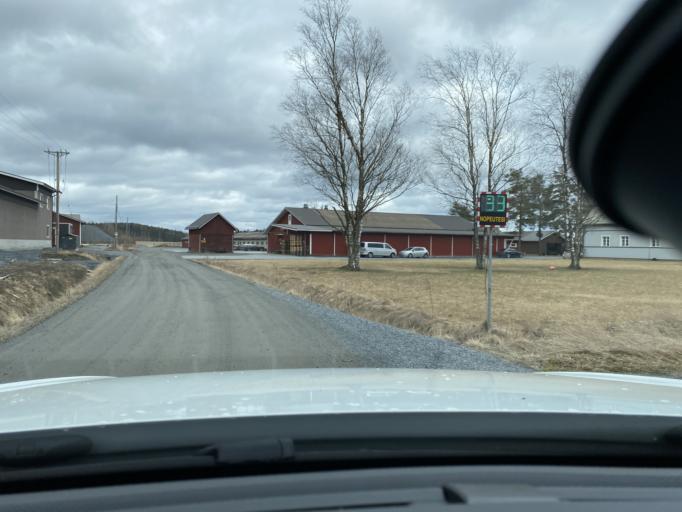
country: FI
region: Pirkanmaa
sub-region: Lounais-Pirkanmaa
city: Punkalaidun
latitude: 61.0899
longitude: 23.2306
